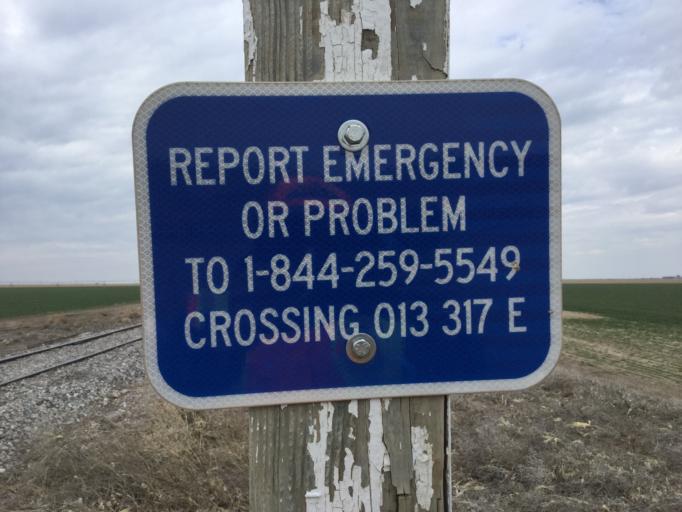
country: US
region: Kansas
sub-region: Stanton County
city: Johnson
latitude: 37.5625
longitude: -101.6175
